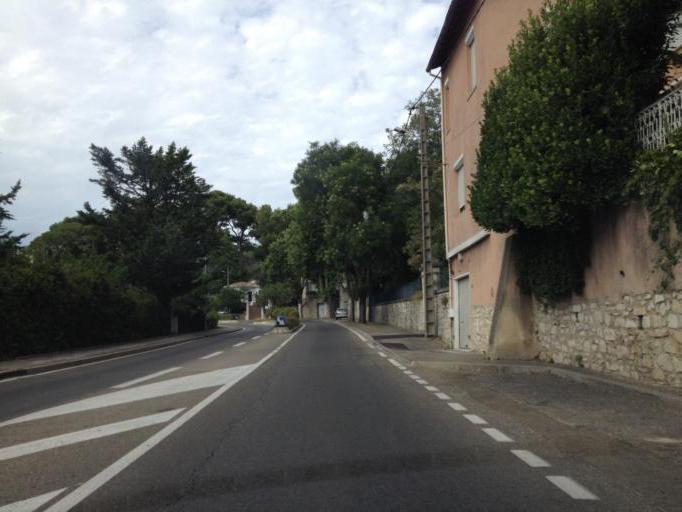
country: FR
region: Languedoc-Roussillon
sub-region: Departement du Gard
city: Villeneuve-les-Avignon
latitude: 43.9553
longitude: 4.7835
